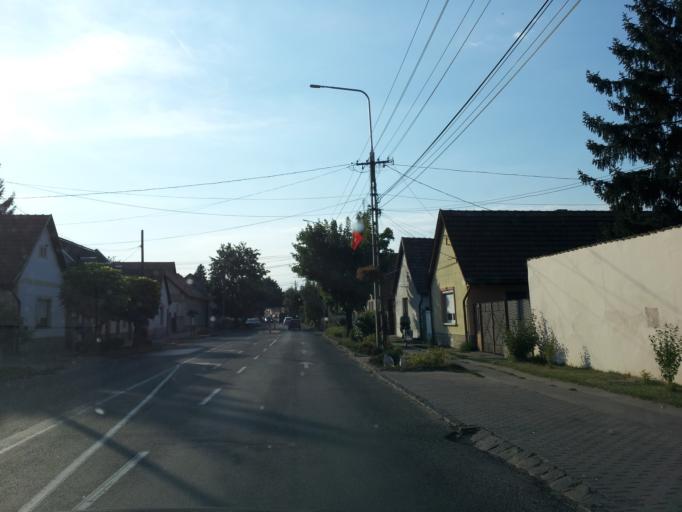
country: HU
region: Pest
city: Dunabogdany
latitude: 47.7945
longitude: 19.0350
